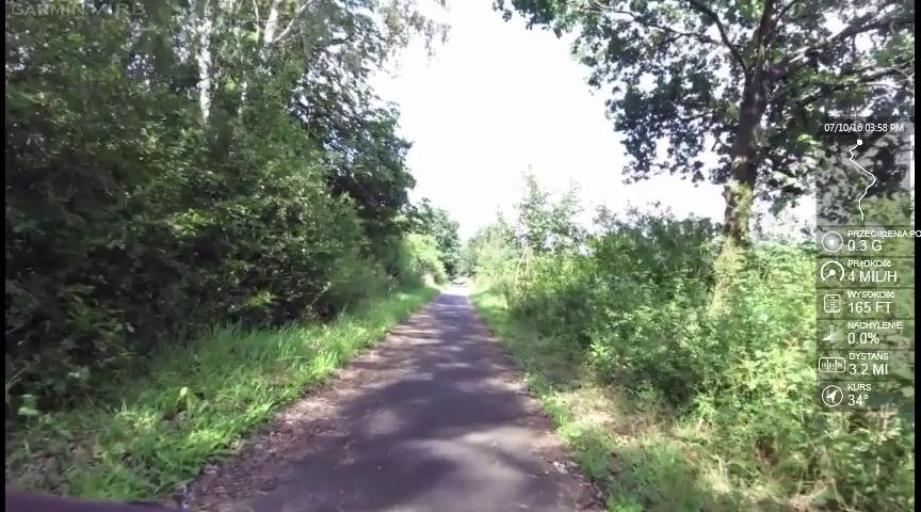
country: PL
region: West Pomeranian Voivodeship
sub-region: Powiat gryfinski
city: Banie
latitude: 53.1516
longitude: 14.6272
